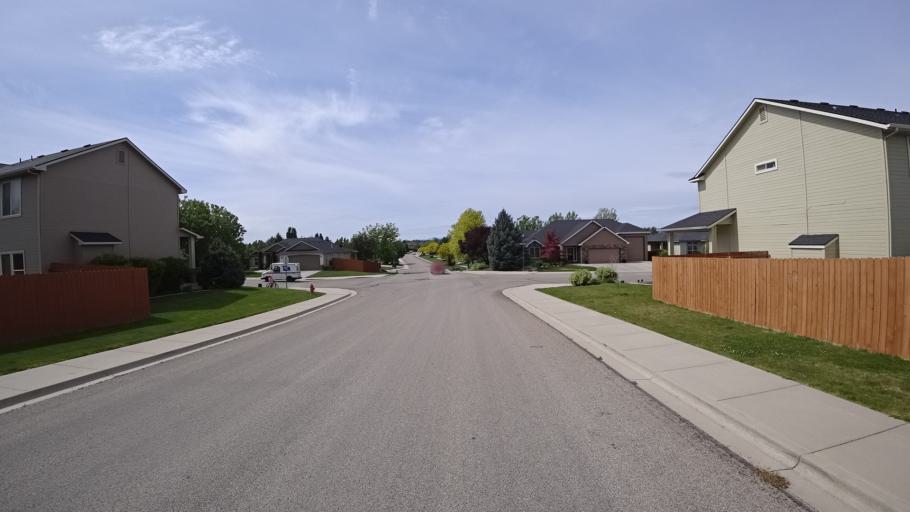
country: US
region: Idaho
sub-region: Ada County
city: Meridian
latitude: 43.5542
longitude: -116.3374
